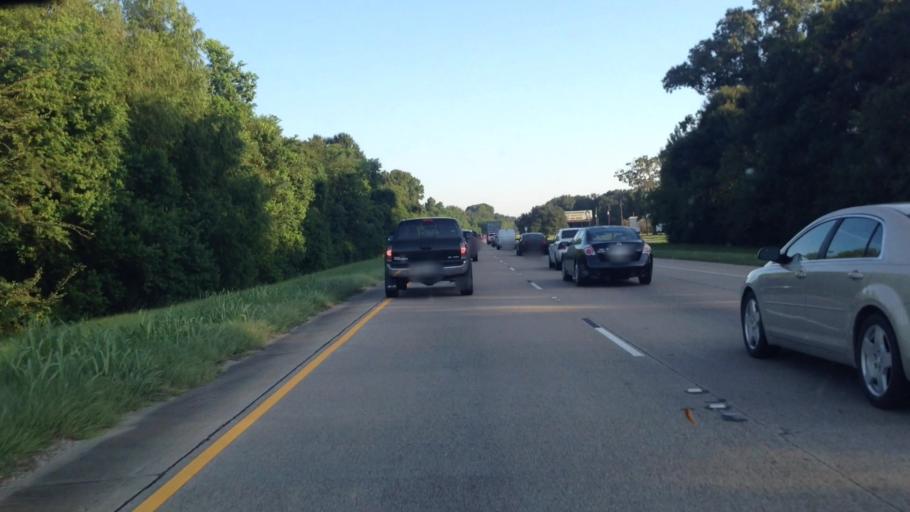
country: US
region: Louisiana
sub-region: Ascension Parish
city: Prairieville
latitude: 30.2760
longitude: -90.9875
